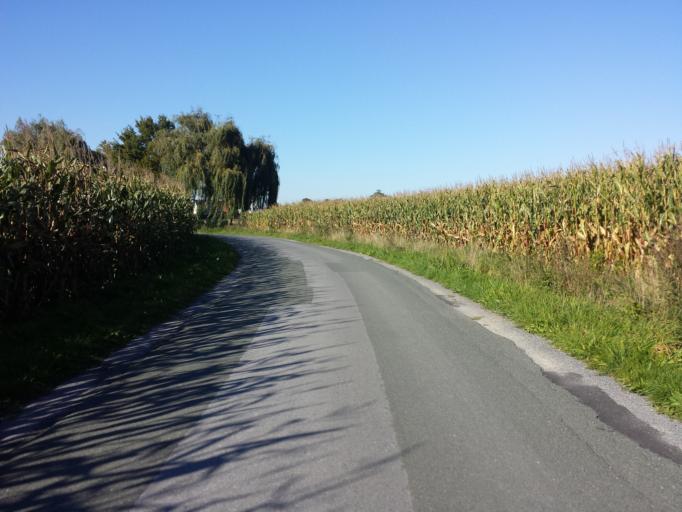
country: DE
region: North Rhine-Westphalia
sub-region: Regierungsbezirk Detmold
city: Langenberg
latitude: 51.7425
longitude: 8.3266
